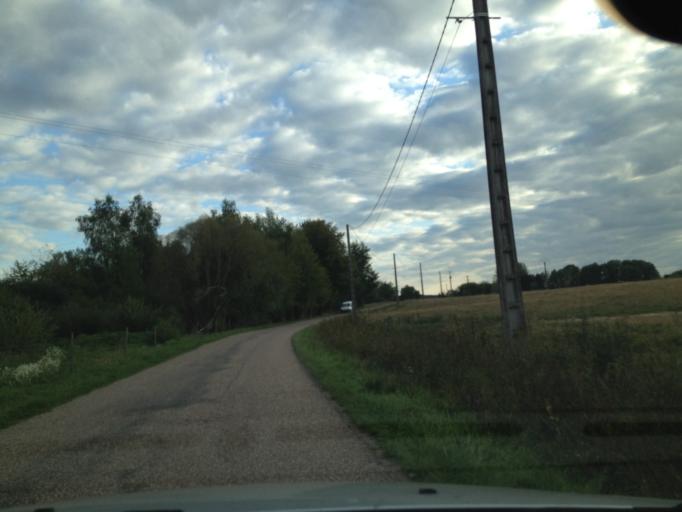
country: FR
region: Lorraine
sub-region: Departement des Vosges
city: Bains-les-Bains
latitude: 47.9950
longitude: 6.2107
